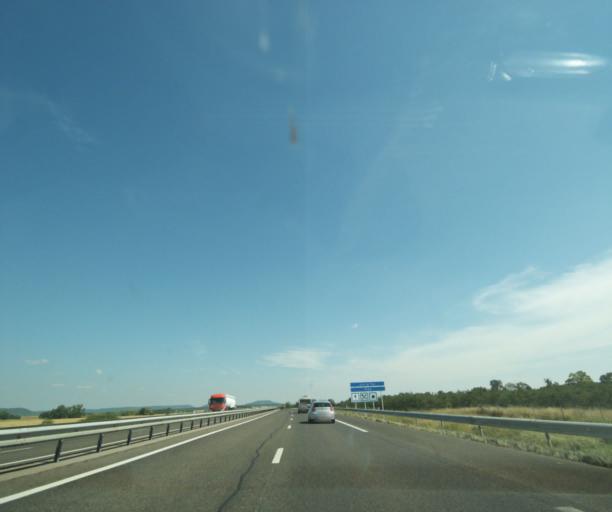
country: FR
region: Lorraine
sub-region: Departement de Meurthe-et-Moselle
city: Blenod-les-Toul
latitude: 48.5874
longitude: 5.8885
